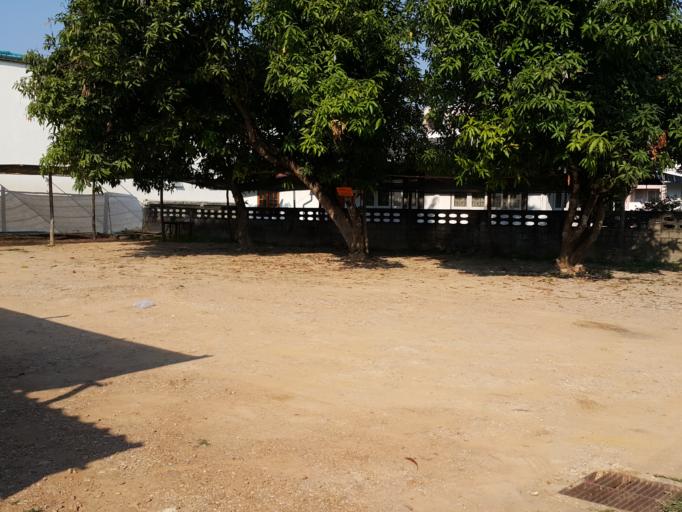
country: TH
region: Lampang
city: Lampang
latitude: 18.2859
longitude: 99.5090
